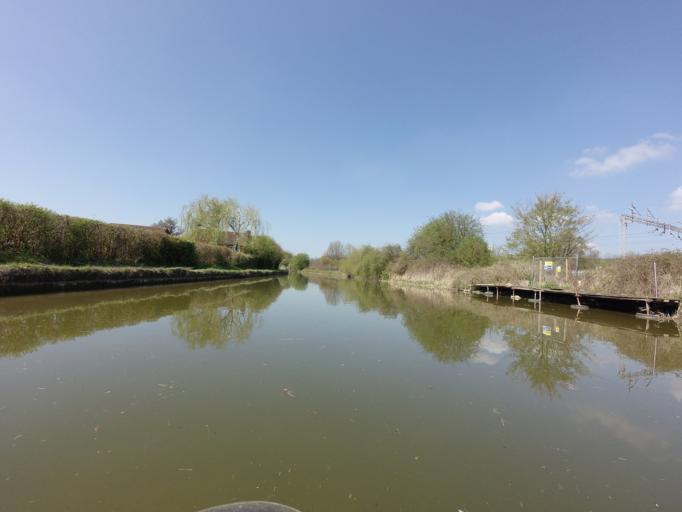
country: GB
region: England
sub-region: Hertfordshire
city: Berkhamsted
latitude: 51.7735
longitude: -0.5901
